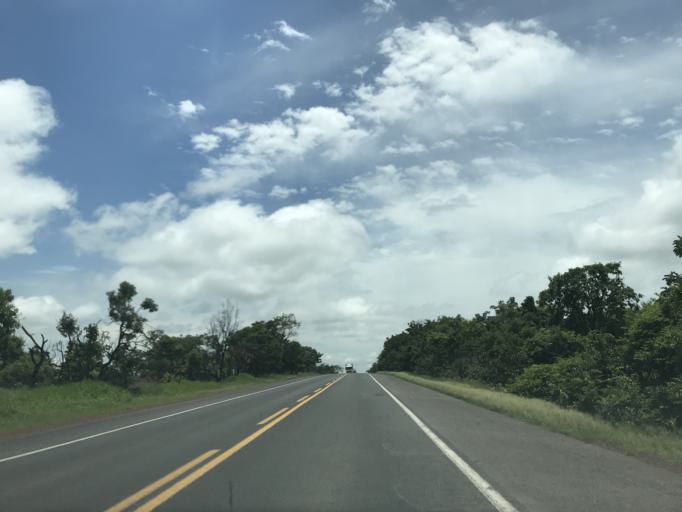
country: BR
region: Minas Gerais
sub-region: Prata
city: Prata
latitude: -19.6282
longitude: -48.9374
